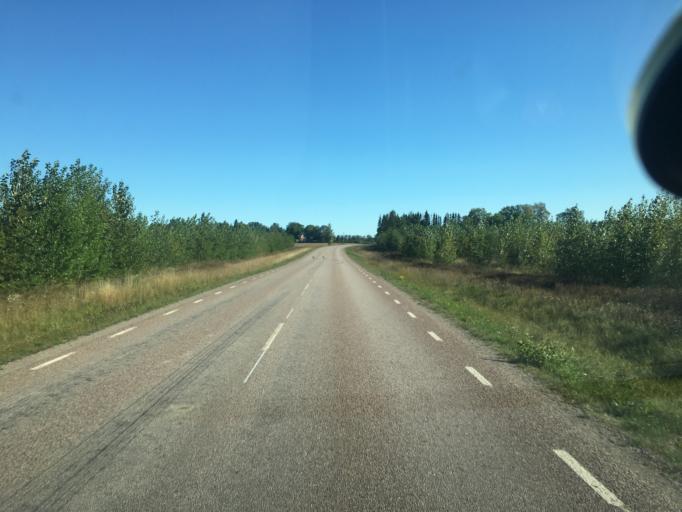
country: SE
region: Vaestmanland
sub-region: Vasteras
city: Tillberga
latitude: 59.6909
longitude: 16.6199
